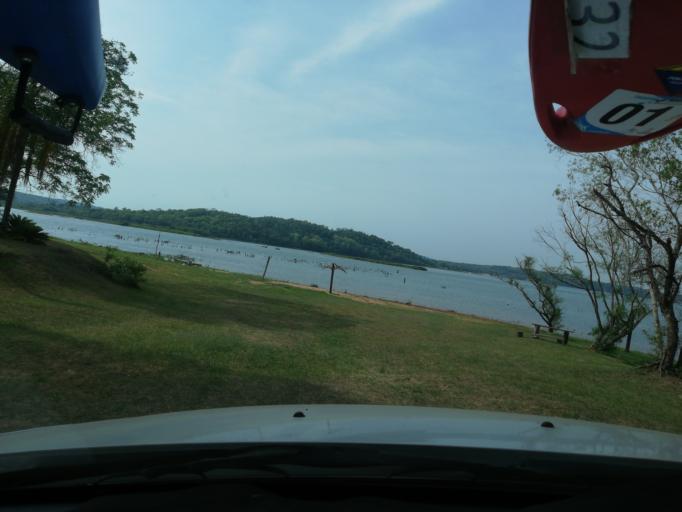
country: AR
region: Misiones
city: Santa Ana
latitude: -27.3095
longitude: -55.5860
